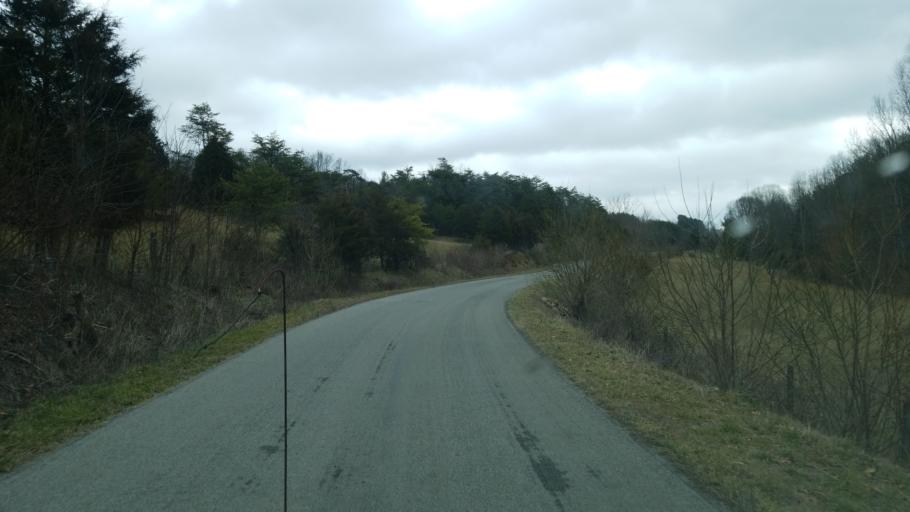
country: US
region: Virginia
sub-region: Giles County
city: Pembroke
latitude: 37.2356
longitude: -80.6919
